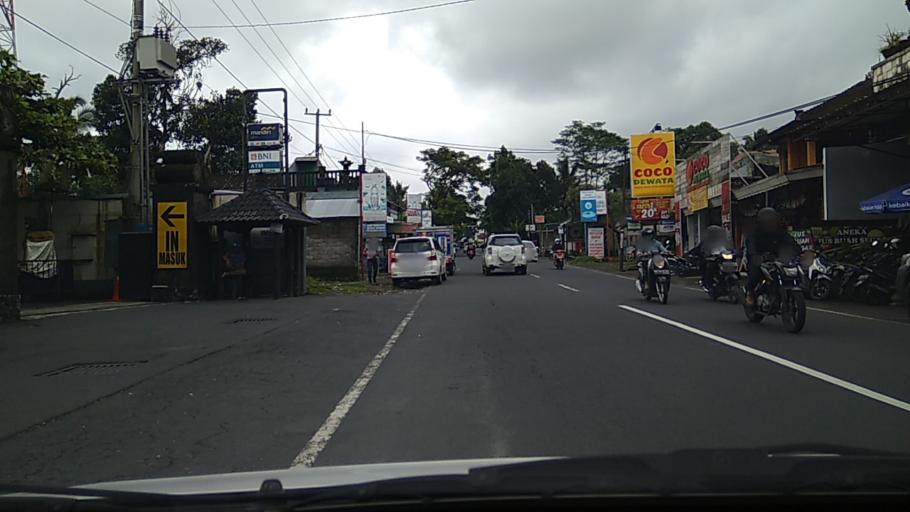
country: ID
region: Bali
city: Peneng
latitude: -8.3870
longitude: 115.1952
